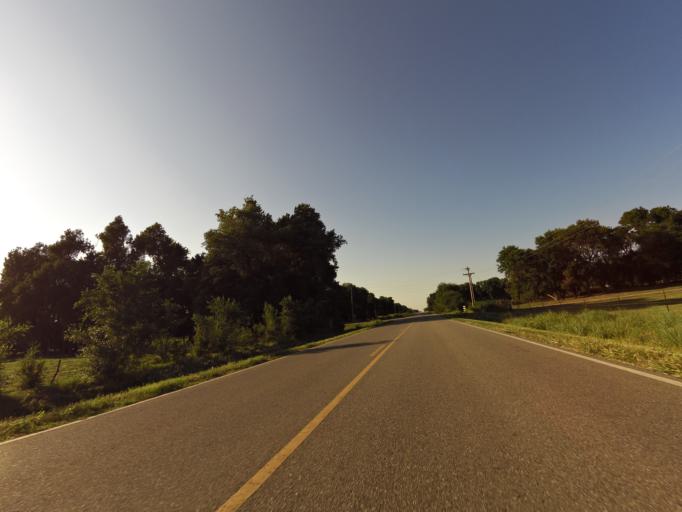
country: US
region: Kansas
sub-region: Reno County
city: Buhler
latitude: 38.1584
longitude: -97.8487
